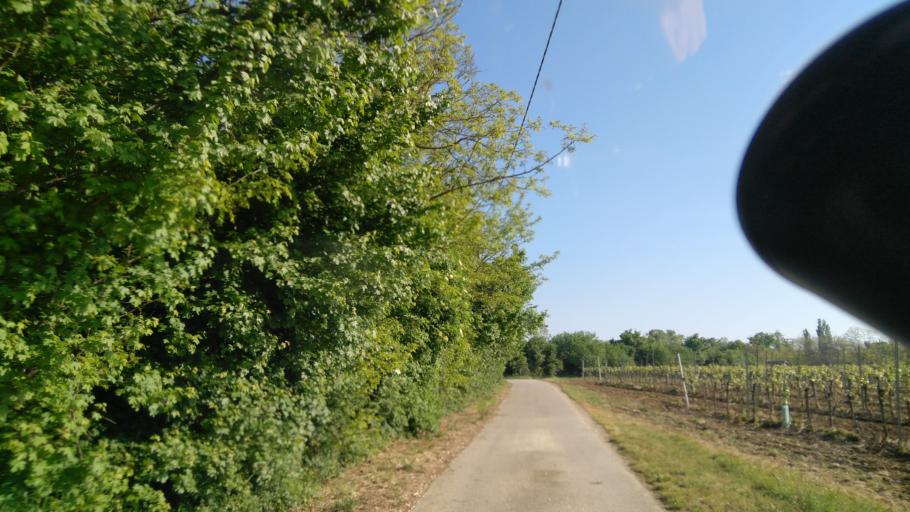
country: HU
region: Zala
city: Sarmellek
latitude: 46.7552
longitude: 17.1416
